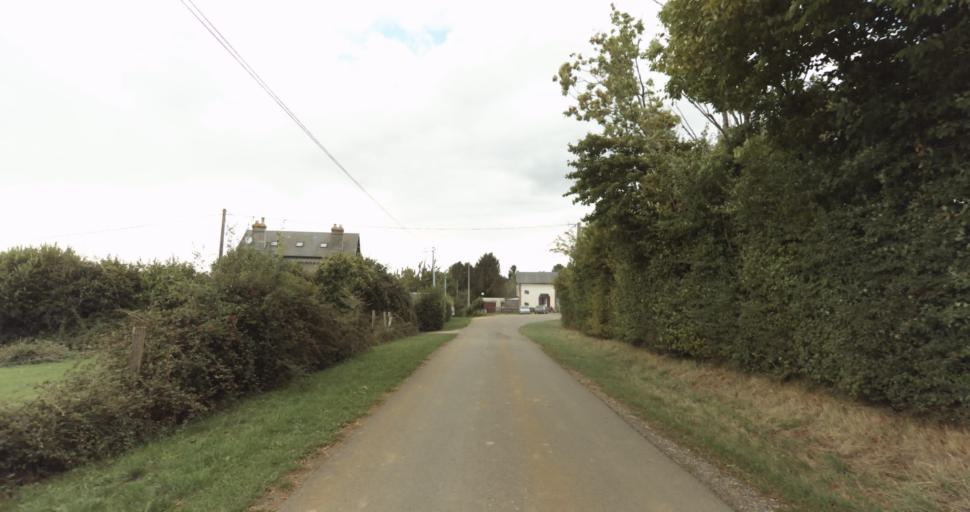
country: FR
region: Lower Normandy
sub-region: Departement de l'Orne
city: Sainte-Gauburge-Sainte-Colombe
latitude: 48.7277
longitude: 0.3953
